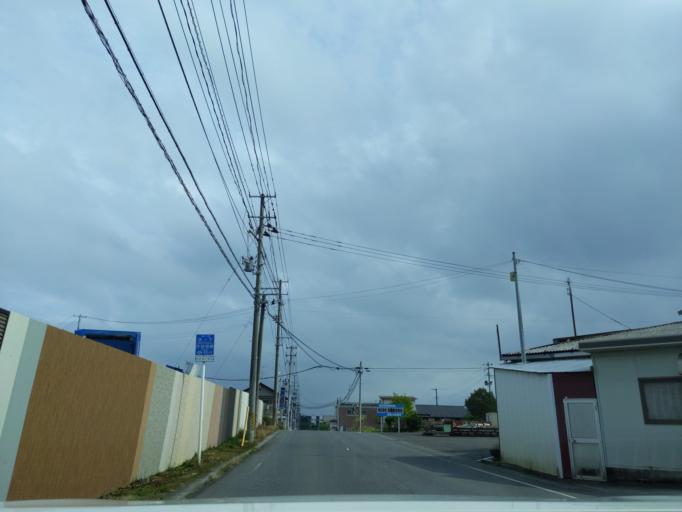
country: JP
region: Fukushima
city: Sukagawa
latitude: 37.3158
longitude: 140.3586
